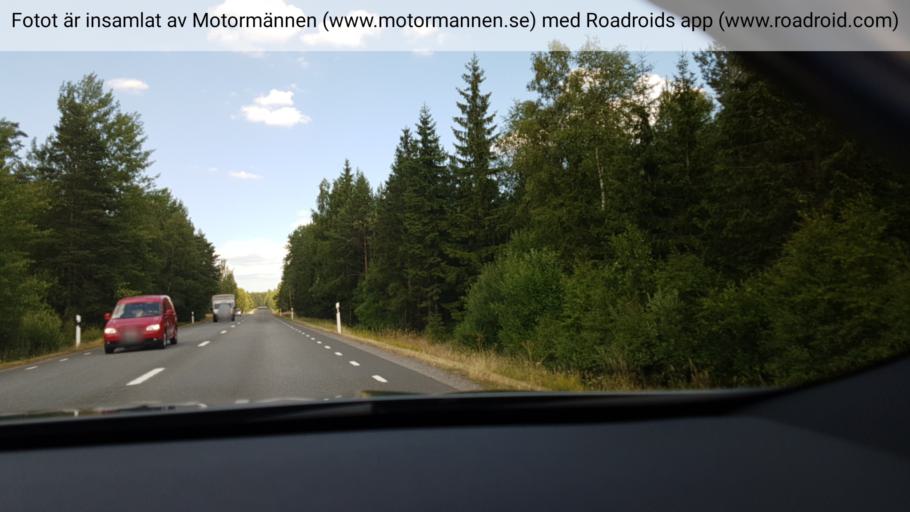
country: SE
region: Joenkoeping
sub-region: Vetlanda Kommun
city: Landsbro
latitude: 57.4038
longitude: 14.9528
